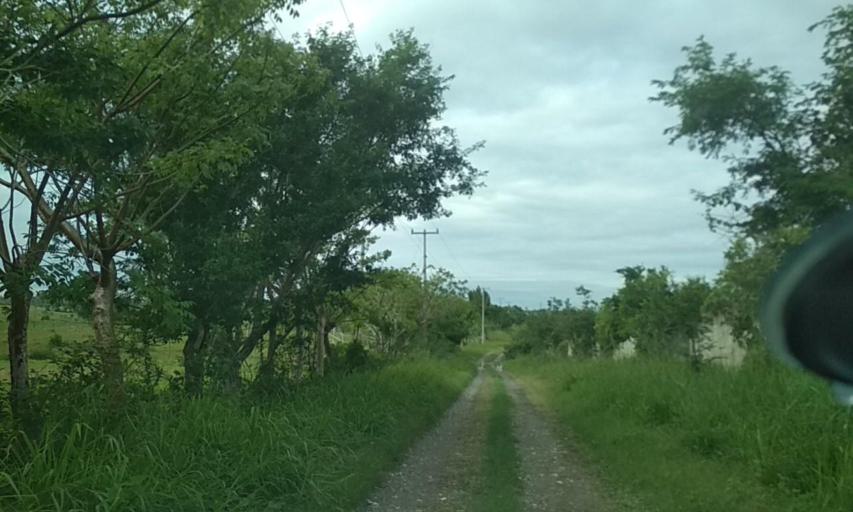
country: MX
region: Veracruz
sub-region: Cazones de Herrera
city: Rancho Nuevo
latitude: 20.6024
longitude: -97.1425
